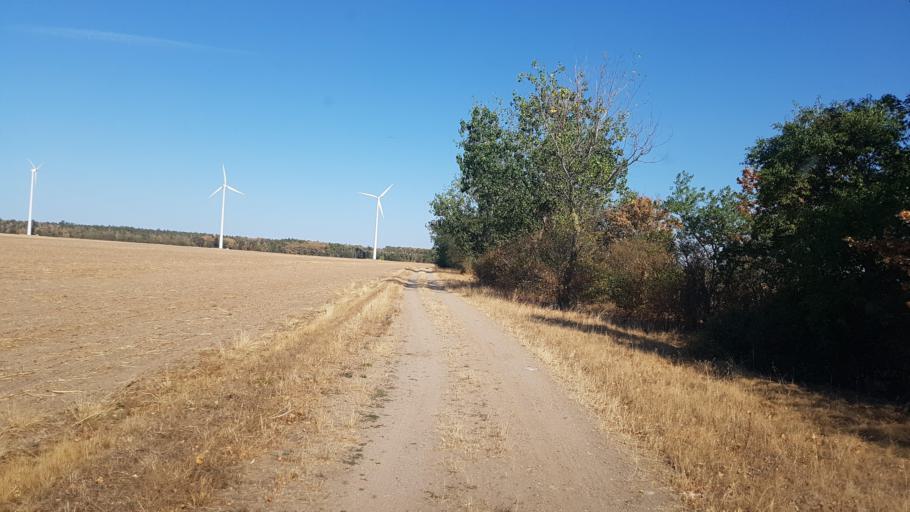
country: DE
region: Brandenburg
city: Muhlberg
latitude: 51.4057
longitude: 13.2742
